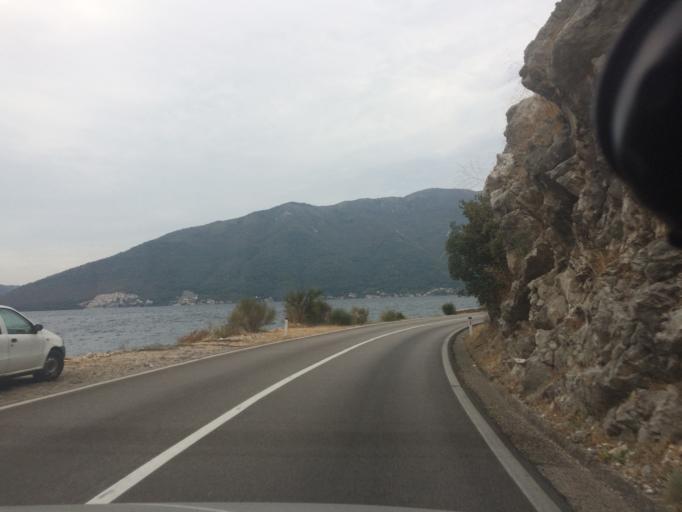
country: ME
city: Lipci
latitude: 42.5059
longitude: 18.6768
